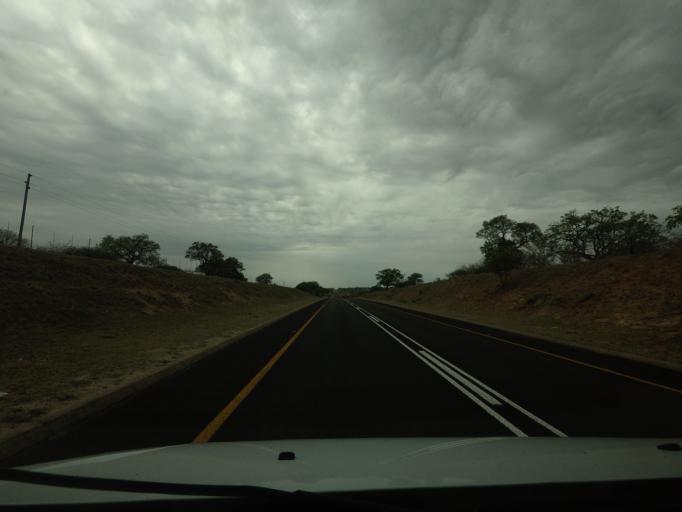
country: ZA
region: Limpopo
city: Thulamahashi
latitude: -24.5641
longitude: 31.1300
